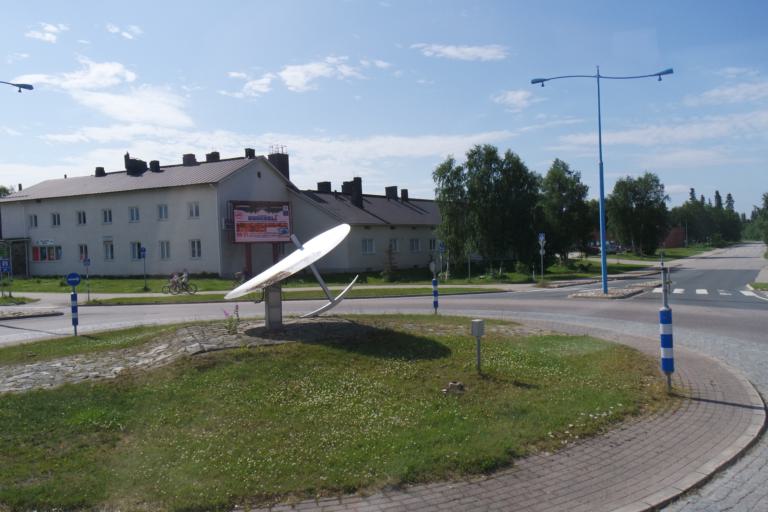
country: FI
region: Lapland
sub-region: Pohjois-Lappi
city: Ivalo
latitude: 68.6565
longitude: 27.5407
